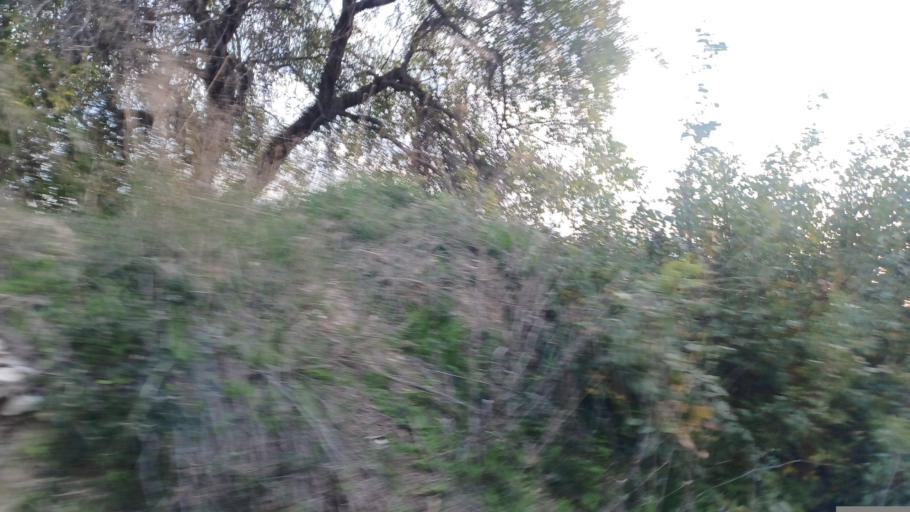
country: CY
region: Pafos
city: Mesogi
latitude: 34.8663
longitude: 32.5139
